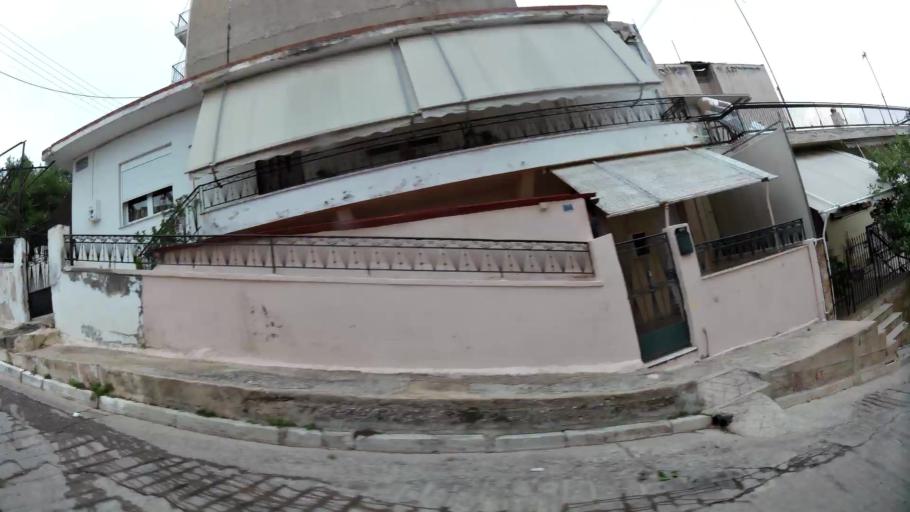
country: GR
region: Attica
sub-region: Nomos Piraios
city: Keratsini
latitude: 37.9785
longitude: 23.6256
